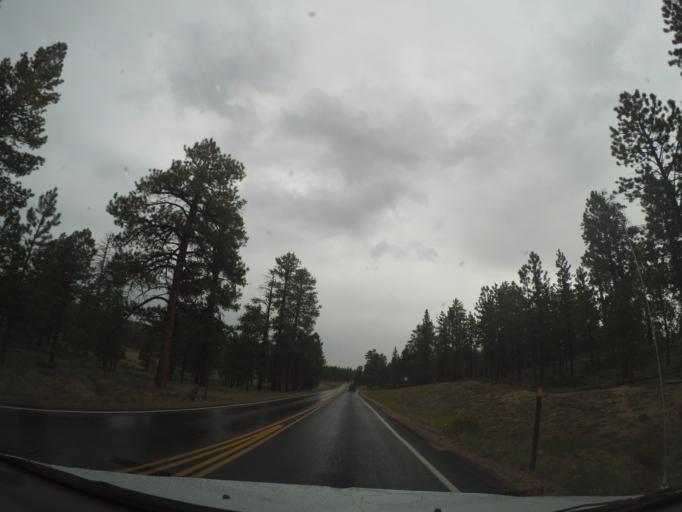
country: US
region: Utah
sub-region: Garfield County
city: Panguitch
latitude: 37.6255
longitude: -112.1715
